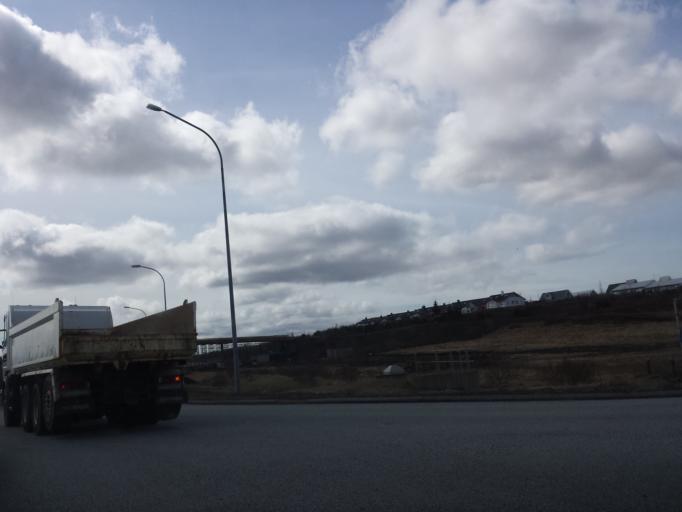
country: IS
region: Capital Region
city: Mosfellsbaer
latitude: 64.1049
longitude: -21.7747
